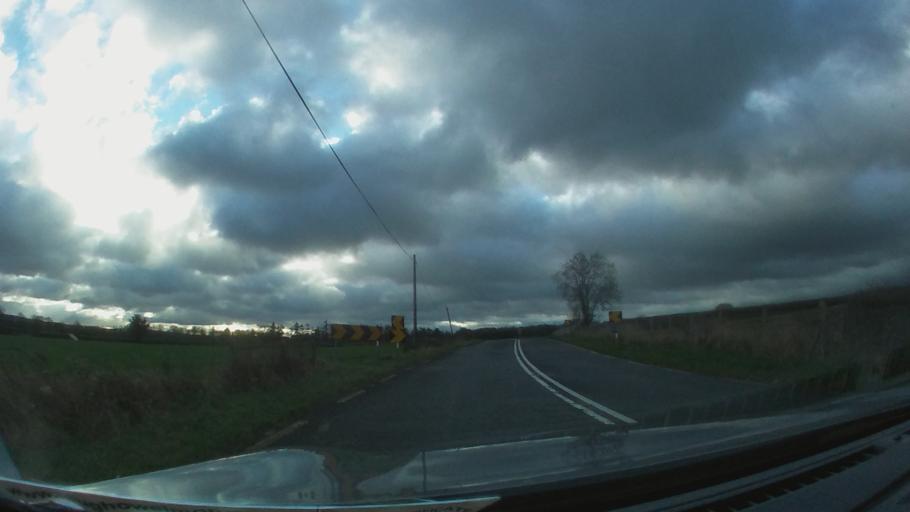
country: IE
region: Leinster
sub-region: Kilkenny
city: Thomastown
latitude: 52.5722
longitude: -7.1134
